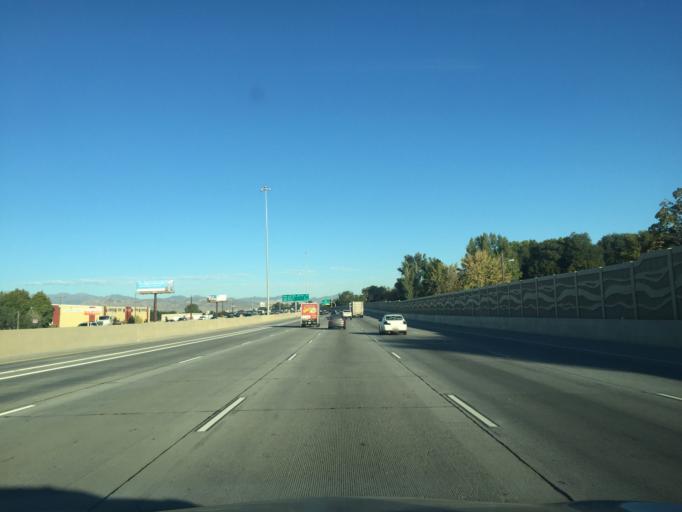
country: US
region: Utah
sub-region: Utah County
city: American Fork
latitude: 40.3689
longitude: -111.7982
